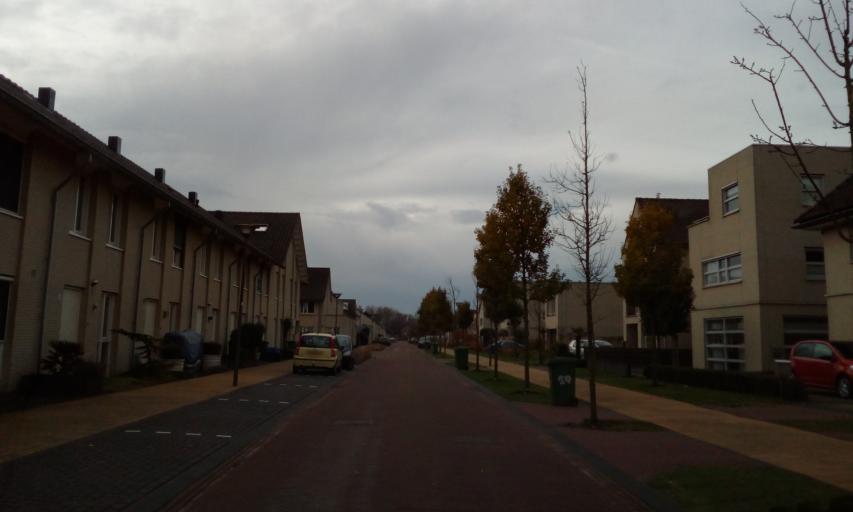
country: NL
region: South Holland
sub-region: Gemeente Rotterdam
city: Hoek van Holland
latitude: 51.9925
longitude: 4.1331
